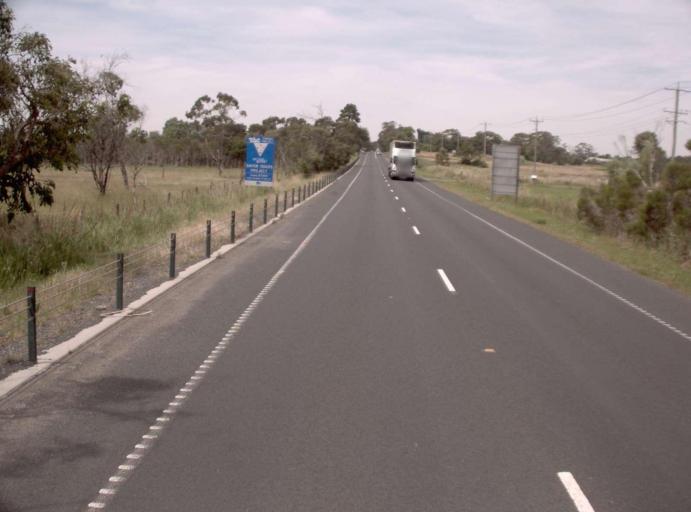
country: AU
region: Victoria
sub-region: Mornington Peninsula
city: Tyabb
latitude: -38.2313
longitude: 145.2163
